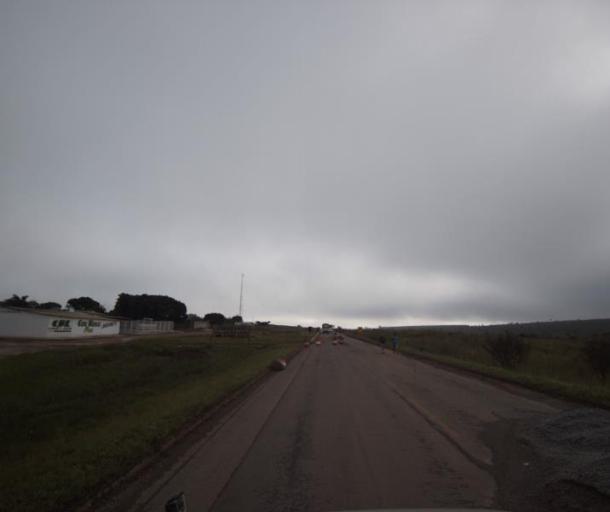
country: BR
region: Goias
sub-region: Pirenopolis
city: Pirenopolis
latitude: -15.7720
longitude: -48.7623
